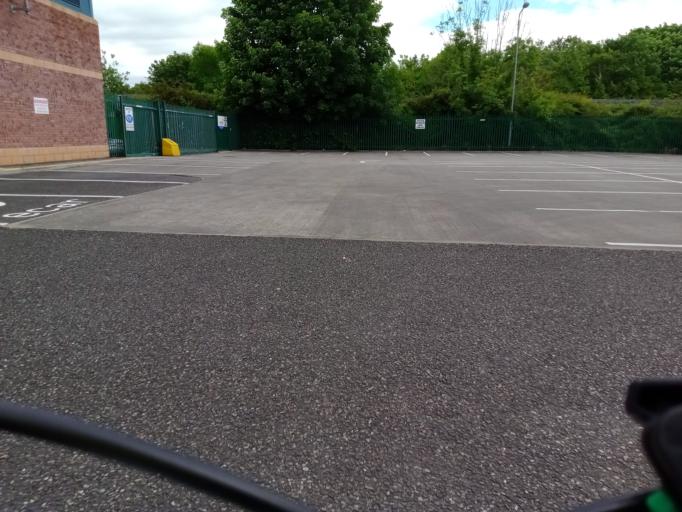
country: IE
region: Leinster
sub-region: Kilkenny
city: Kilkenny
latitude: 52.6482
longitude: -7.2200
